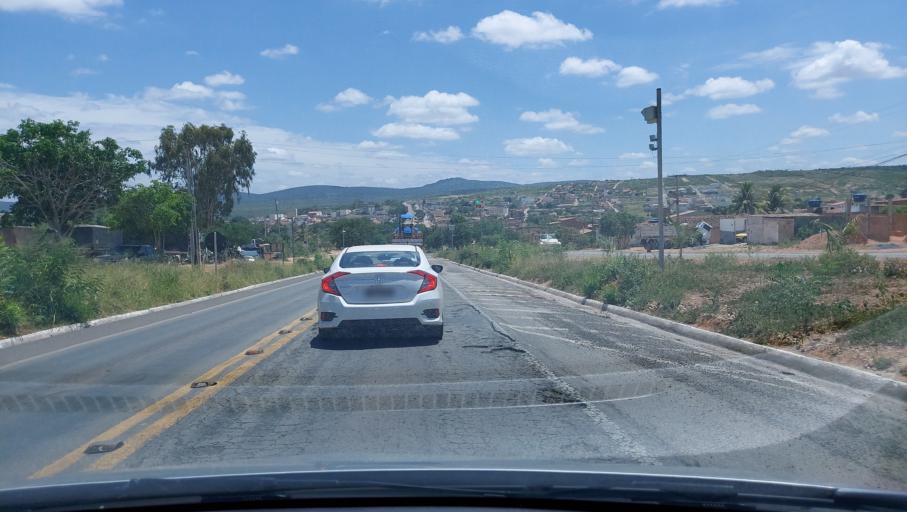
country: BR
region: Bahia
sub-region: Seabra
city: Seabra
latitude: -12.4290
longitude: -41.7818
